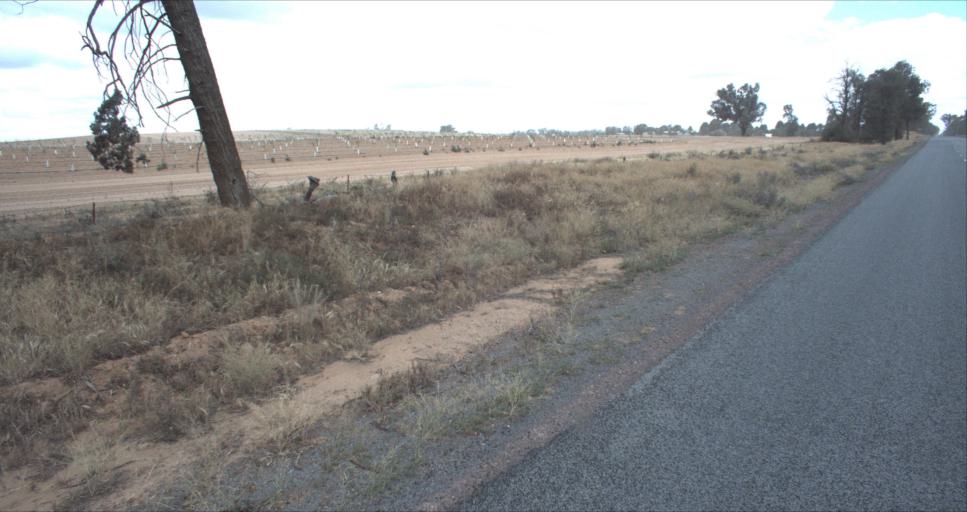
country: AU
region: New South Wales
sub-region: Leeton
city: Leeton
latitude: -34.6565
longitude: 146.3502
